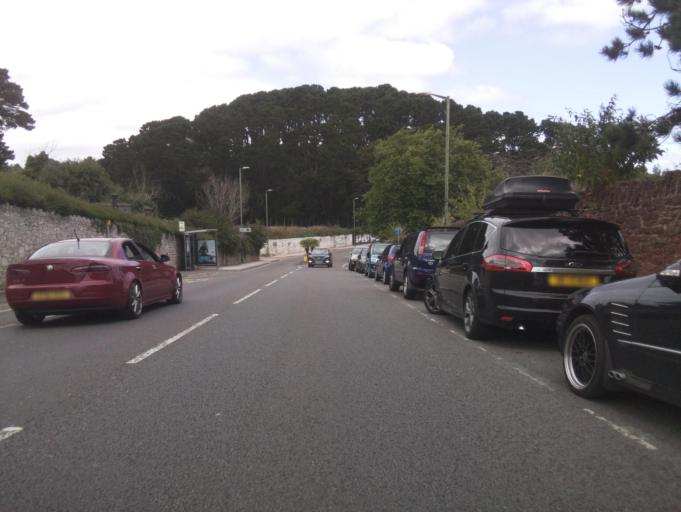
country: GB
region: England
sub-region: Borough of Torbay
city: Paignton
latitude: 50.4501
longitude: -3.5547
